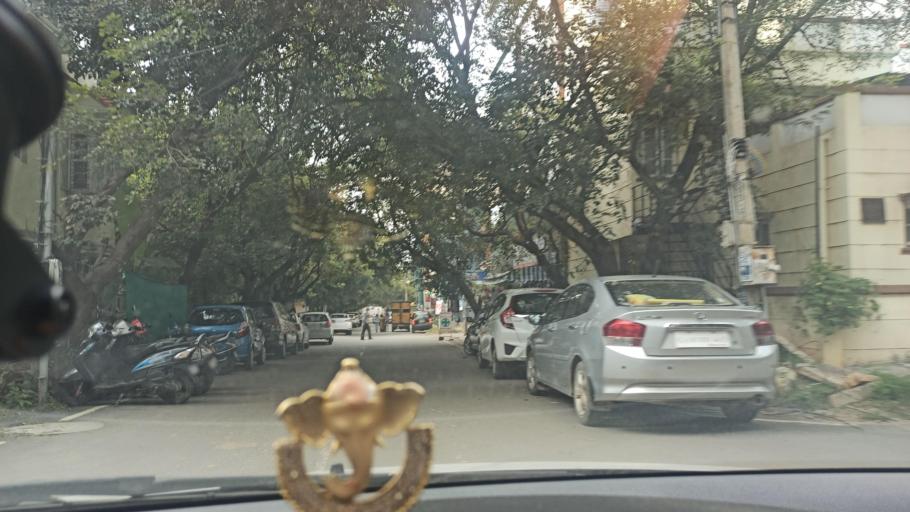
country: IN
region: Karnataka
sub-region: Bangalore Urban
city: Bangalore
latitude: 12.9172
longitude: 77.6441
